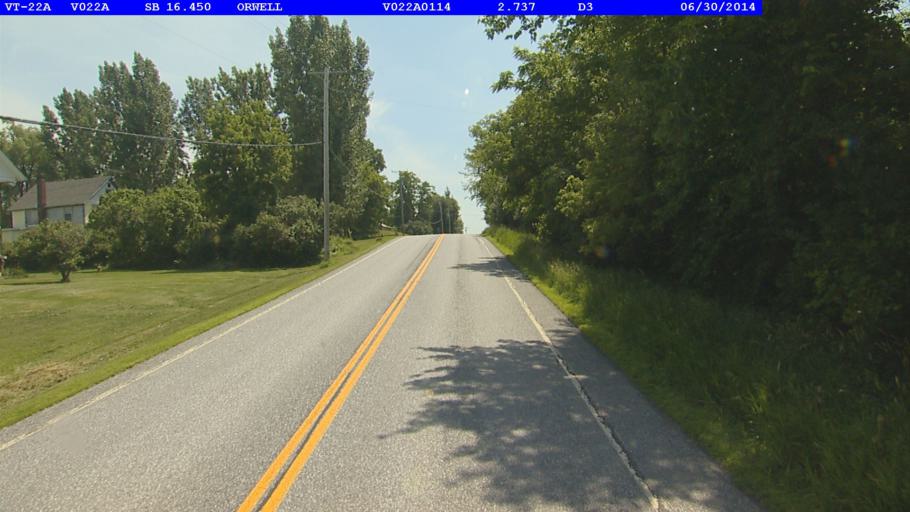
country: US
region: New York
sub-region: Essex County
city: Ticonderoga
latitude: 43.7964
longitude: -73.3062
